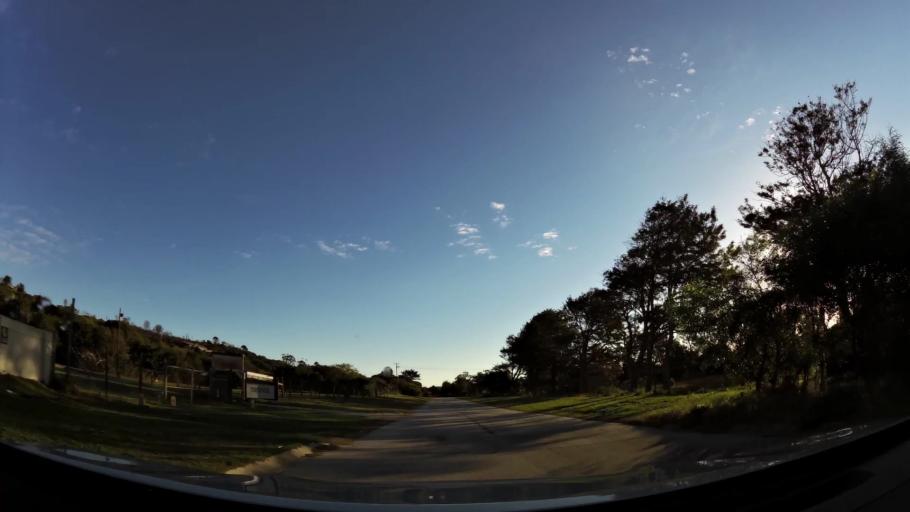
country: ZA
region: Eastern Cape
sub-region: Nelson Mandela Bay Metropolitan Municipality
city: Port Elizabeth
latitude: -33.9853
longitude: 25.4947
